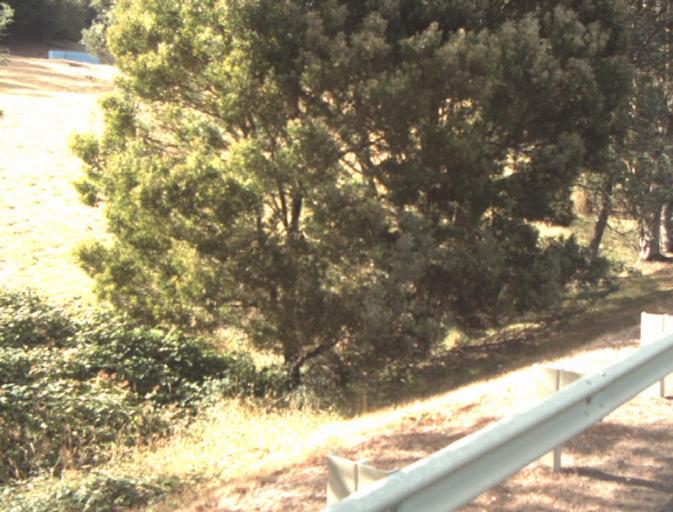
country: AU
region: Tasmania
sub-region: Launceston
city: Mayfield
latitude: -41.2888
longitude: 147.2175
